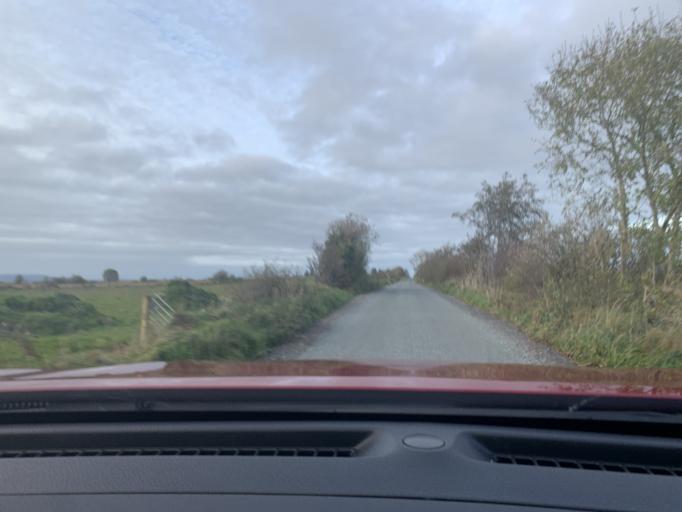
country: IE
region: Connaught
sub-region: Roscommon
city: Ballaghaderreen
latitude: 53.9860
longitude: -8.6143
